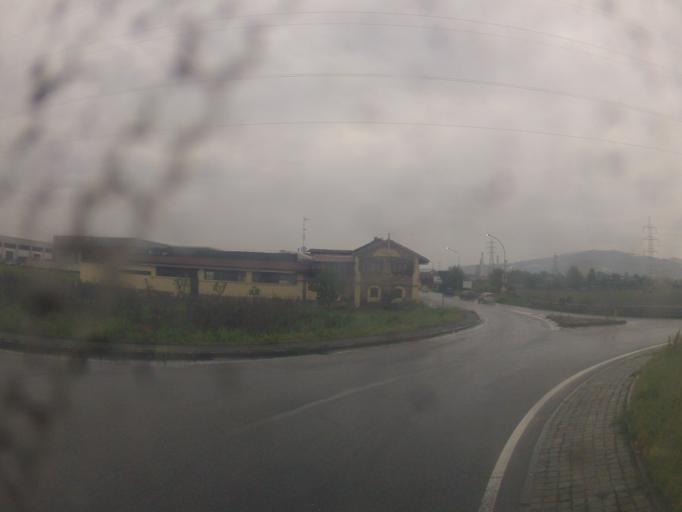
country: IT
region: Piedmont
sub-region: Provincia di Torino
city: Tagliaferro
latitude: 44.9845
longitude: 7.6707
